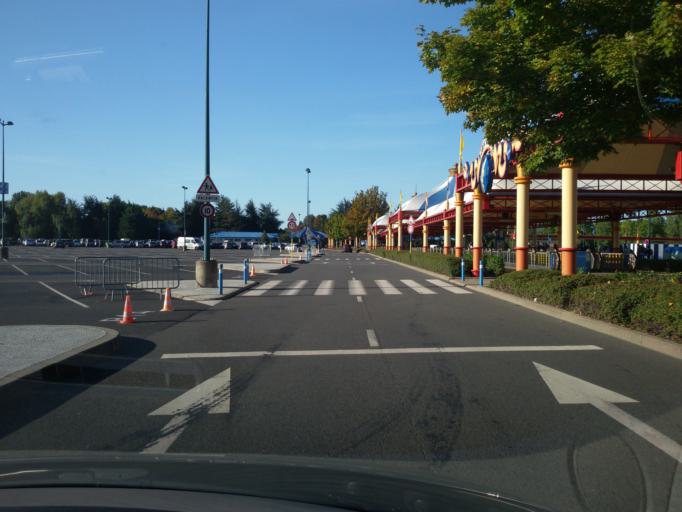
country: FR
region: Ile-de-France
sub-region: Departement de Seine-et-Marne
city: Chalifert
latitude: 48.8746
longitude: 2.7865
